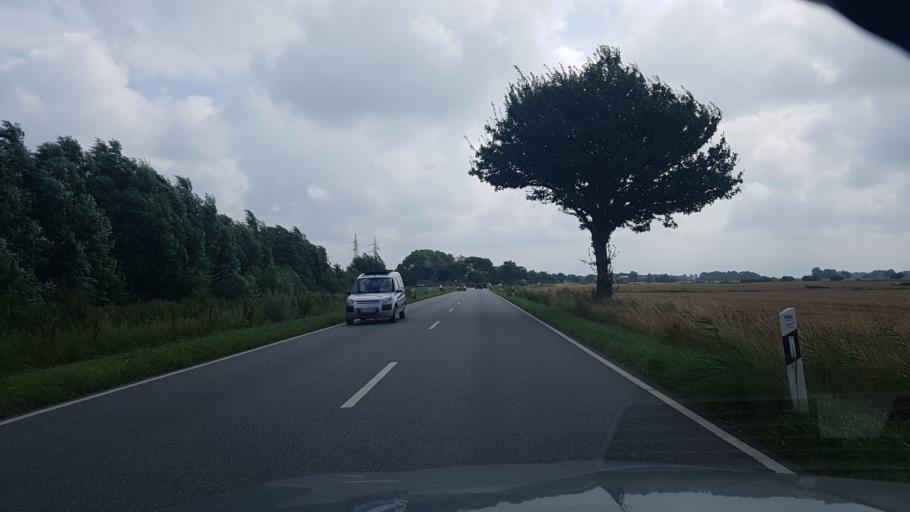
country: DE
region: Schleswig-Holstein
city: Tating
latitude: 54.3276
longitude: 8.7429
